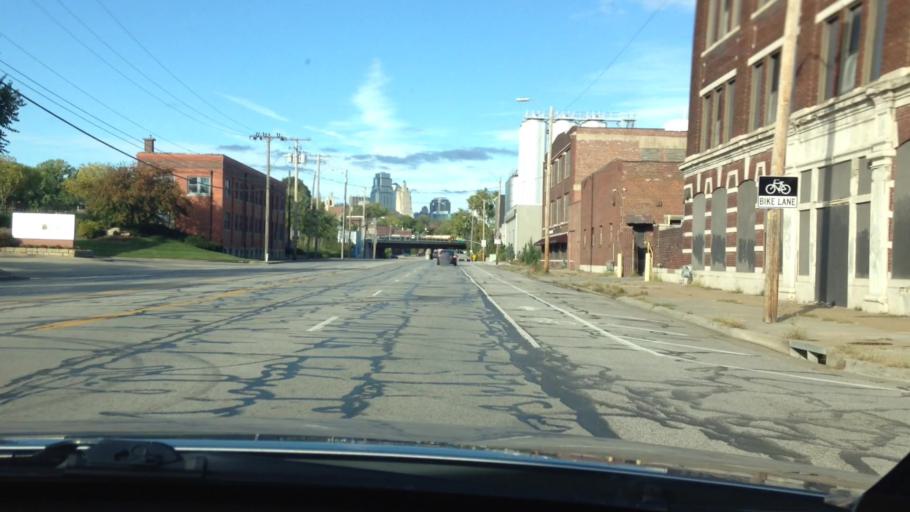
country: US
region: Missouri
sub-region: Jackson County
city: Kansas City
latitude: 39.0809
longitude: -94.5981
